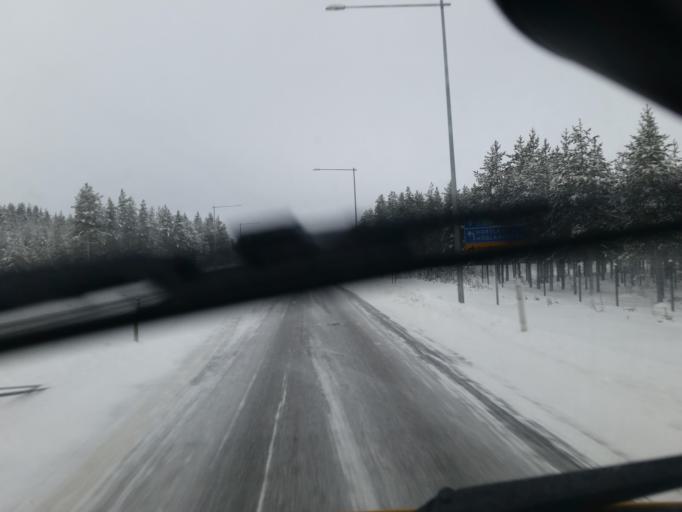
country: SE
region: Norrbotten
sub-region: Pitea Kommun
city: Pitea
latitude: 65.2756
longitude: 21.4515
